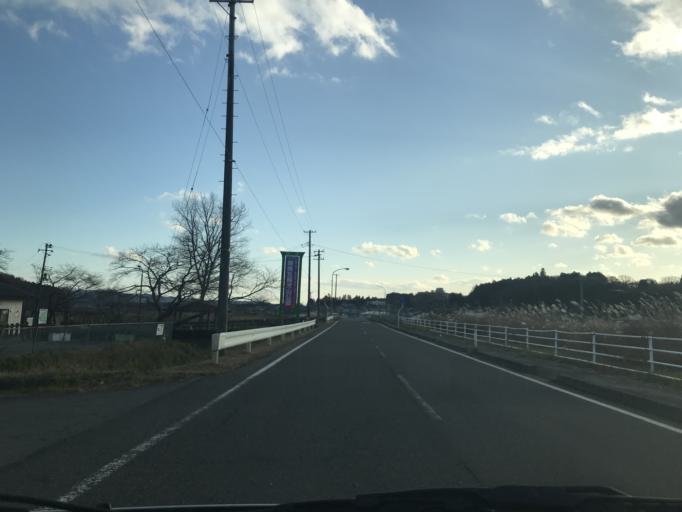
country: JP
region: Miyagi
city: Kogota
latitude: 38.6613
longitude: 141.0736
